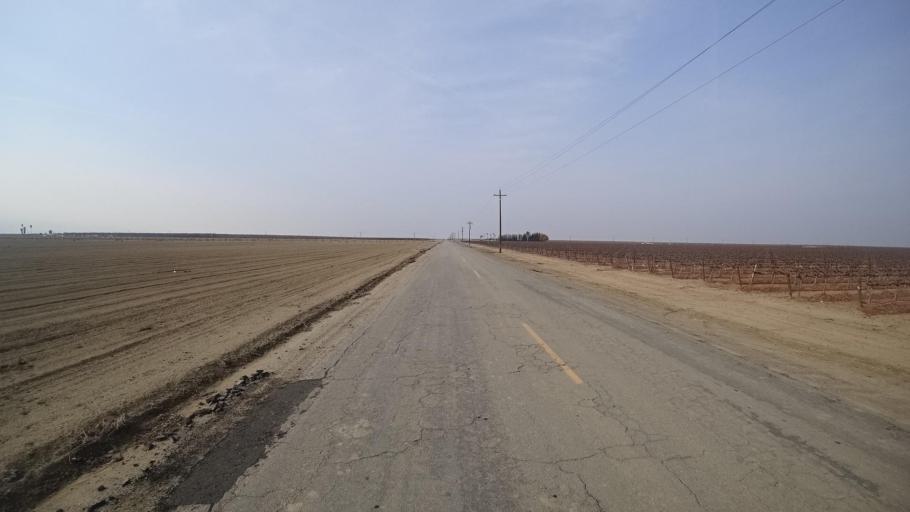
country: US
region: California
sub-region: Kern County
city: Greenfield
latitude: 35.0768
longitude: -119.0944
